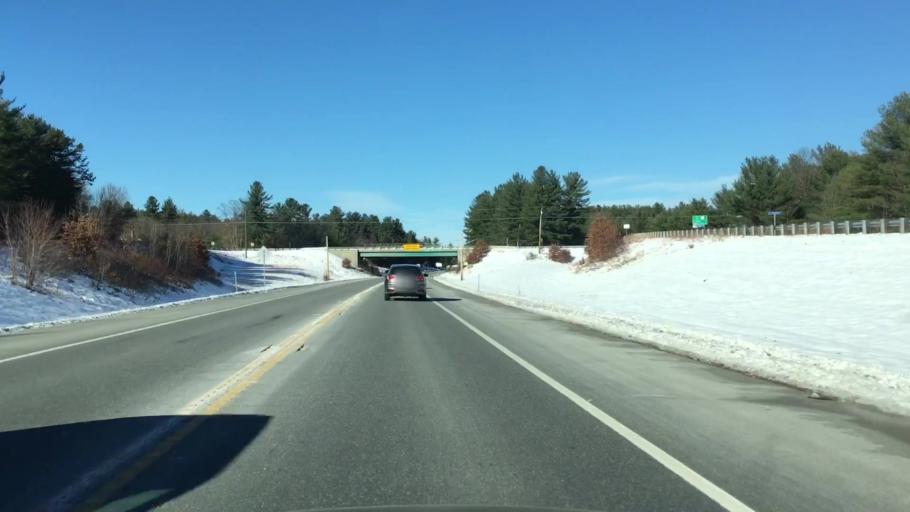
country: US
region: New Hampshire
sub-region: Hillsborough County
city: Milford
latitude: 42.8643
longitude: -71.6133
